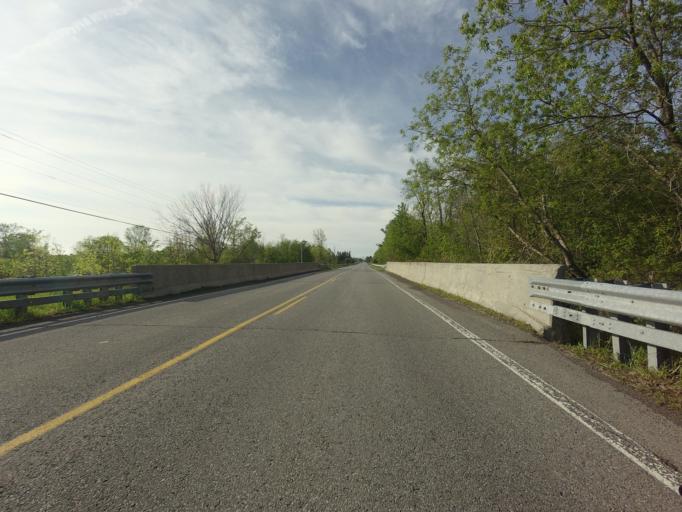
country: CA
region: Ontario
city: Ottawa
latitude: 45.2816
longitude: -75.4438
